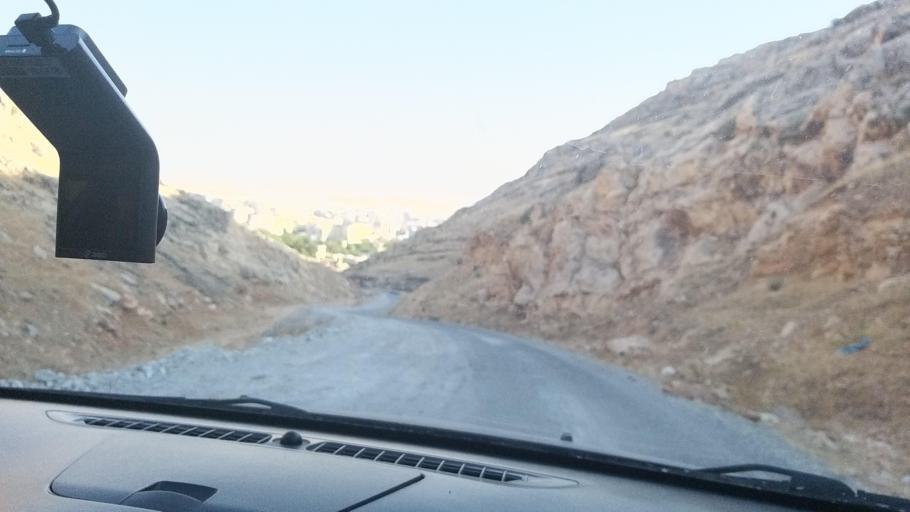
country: TR
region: Diyarbakir
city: Silvan
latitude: 38.1576
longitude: 41.0030
